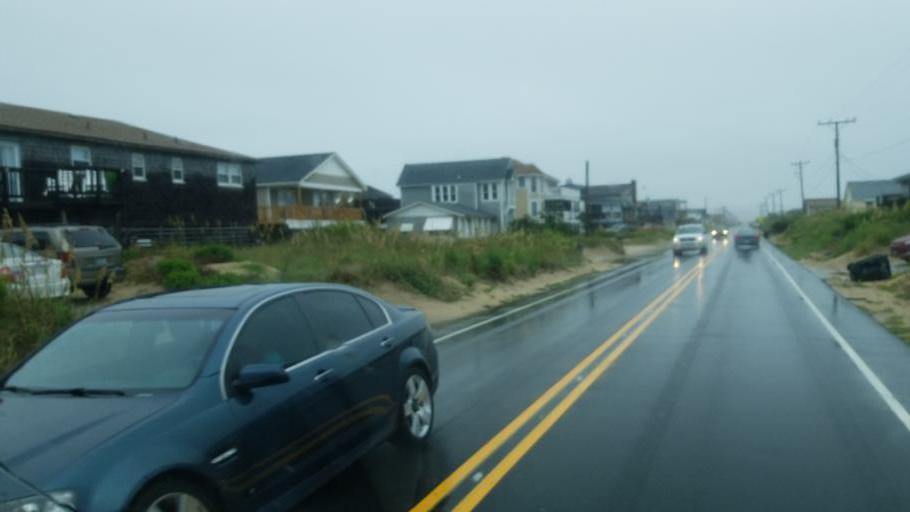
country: US
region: North Carolina
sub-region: Dare County
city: Kitty Hawk
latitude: 36.0596
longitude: -75.6855
